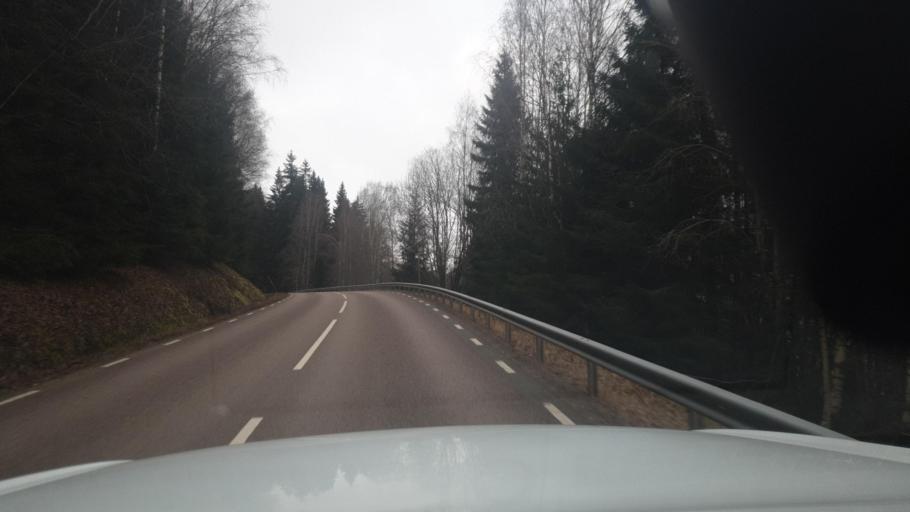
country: SE
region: Vaermland
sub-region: Sunne Kommun
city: Sunne
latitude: 59.8238
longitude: 12.9946
